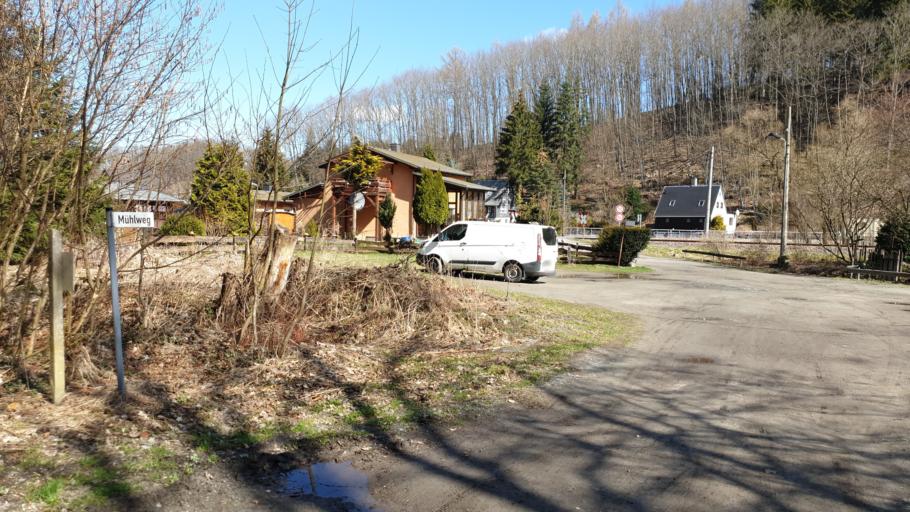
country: DE
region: Saxony
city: Gelenau
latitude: 50.7413
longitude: 12.9819
